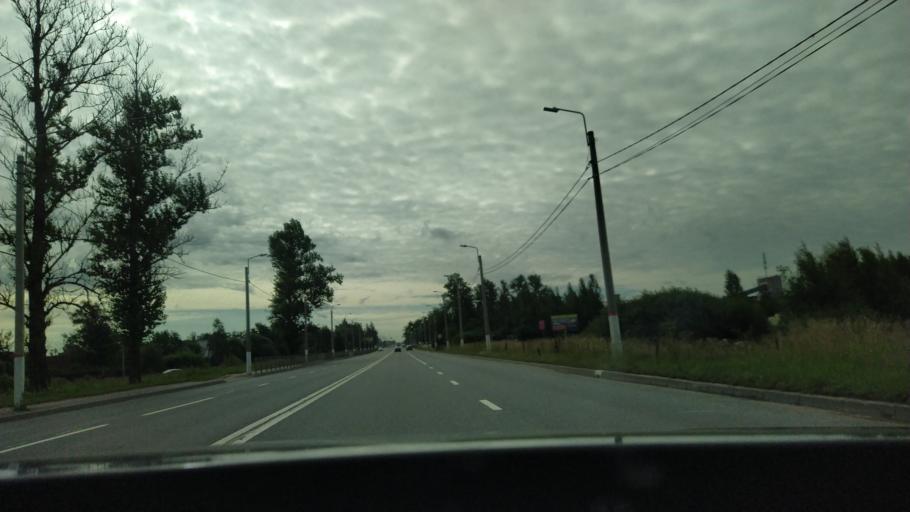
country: RU
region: Leningrad
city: Tosno
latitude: 59.5622
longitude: 30.8382
